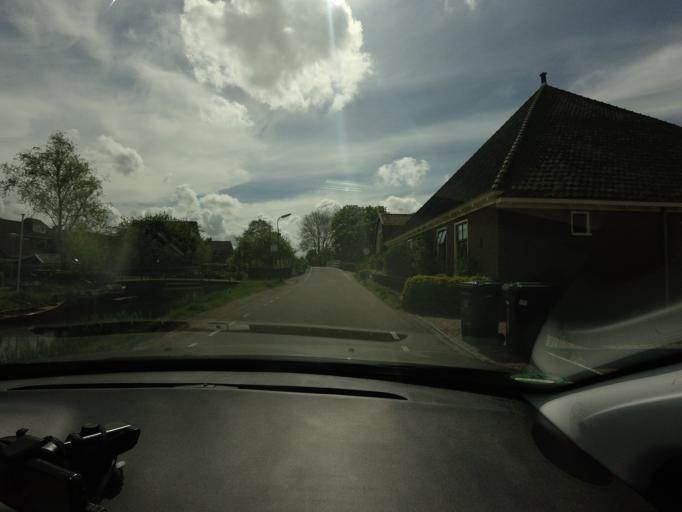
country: NL
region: North Holland
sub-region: Gemeente Beemster
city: Halfweg
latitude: 52.5648
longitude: 4.8326
